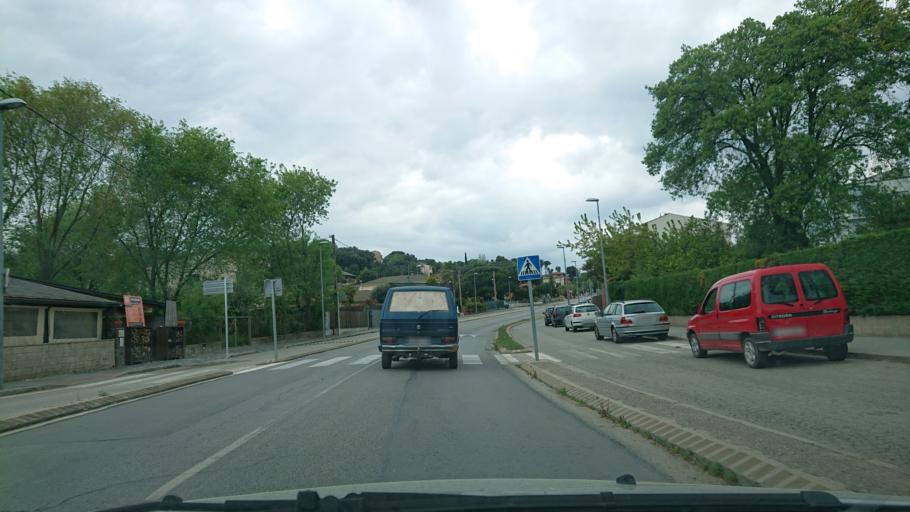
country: ES
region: Catalonia
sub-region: Provincia de Barcelona
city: Sant Pere de Vilamajor
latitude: 41.6735
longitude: 2.3971
